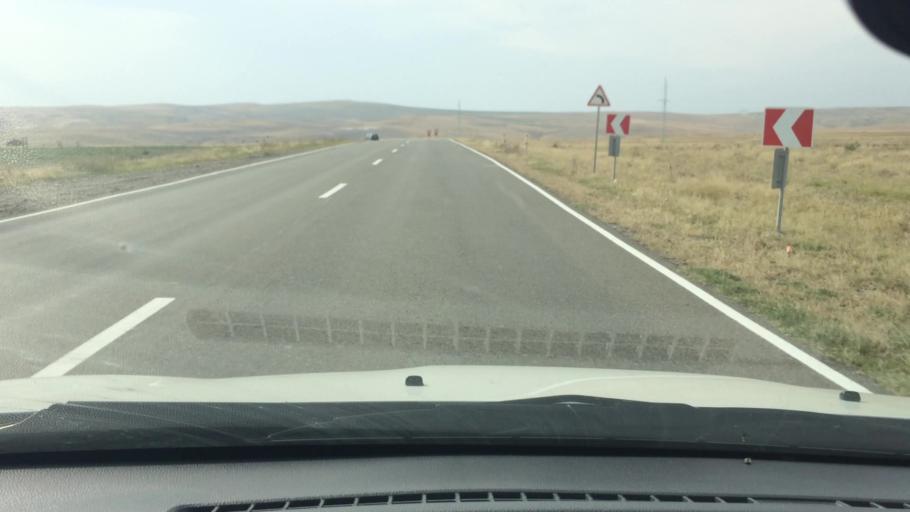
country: GE
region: Kvemo Kartli
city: Rust'avi
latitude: 41.5334
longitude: 44.9466
